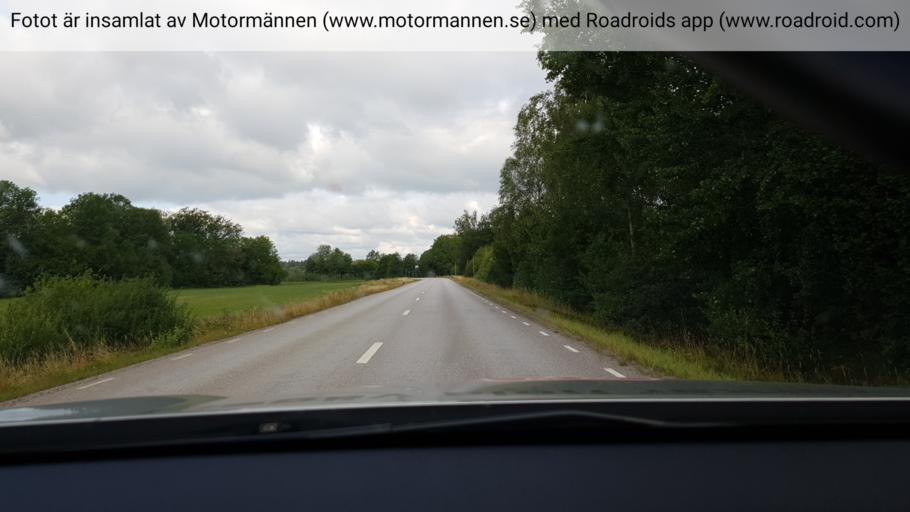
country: SE
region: Stockholm
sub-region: Norrtalje Kommun
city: Skanninge
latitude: 59.8961
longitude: 18.3973
